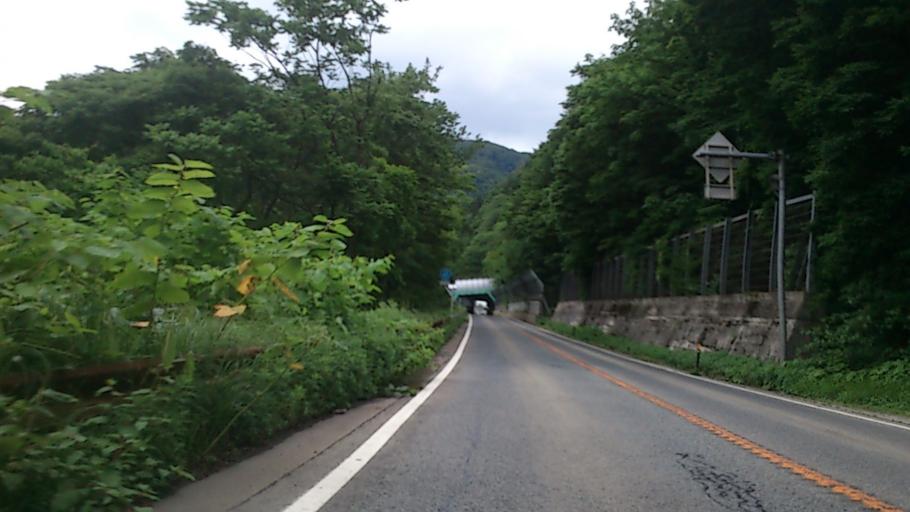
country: JP
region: Yamagata
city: Shinjo
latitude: 38.7501
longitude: 140.0839
